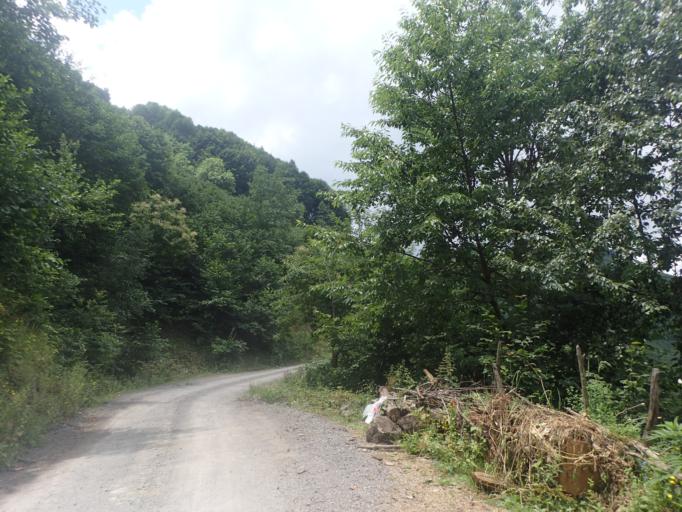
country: TR
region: Ordu
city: Akkus
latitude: 40.8940
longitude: 37.0003
